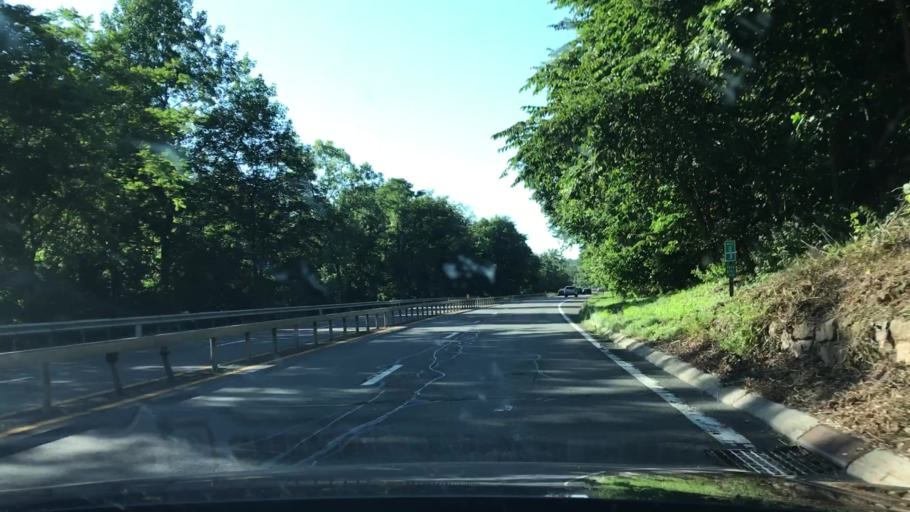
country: US
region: New York
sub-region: Westchester County
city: Valhalla
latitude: 41.0787
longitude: -73.7799
